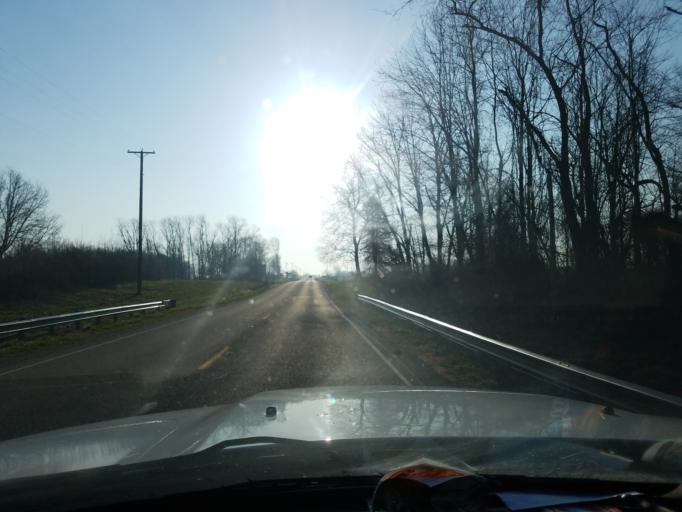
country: US
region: Indiana
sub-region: Vigo County
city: Seelyville
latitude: 39.3902
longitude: -87.2437
